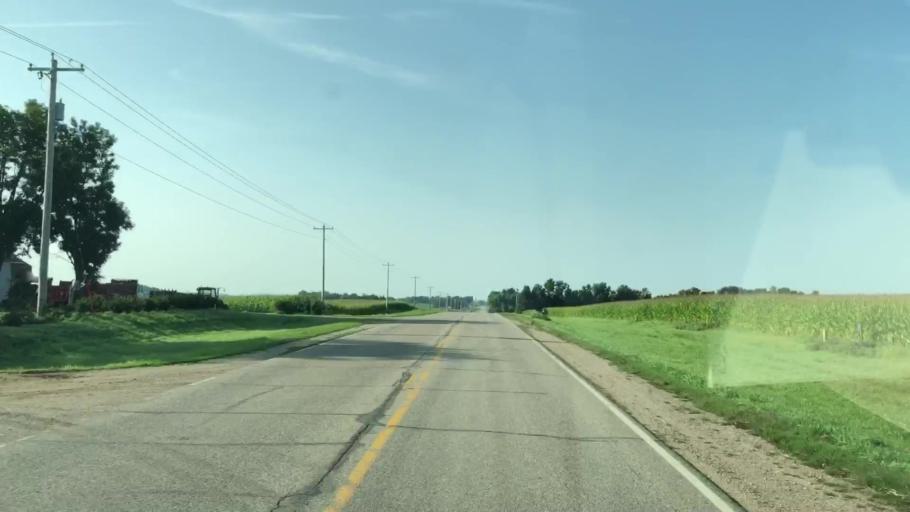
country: US
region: Iowa
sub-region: Lyon County
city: George
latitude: 43.3733
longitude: -95.9982
